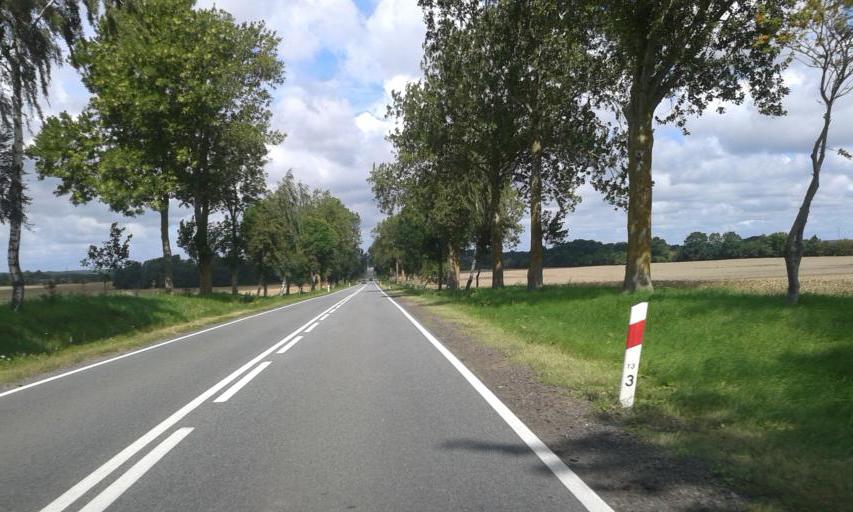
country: PL
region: West Pomeranian Voivodeship
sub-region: Powiat slawienski
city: Slawno
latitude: 54.3354
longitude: 16.5485
